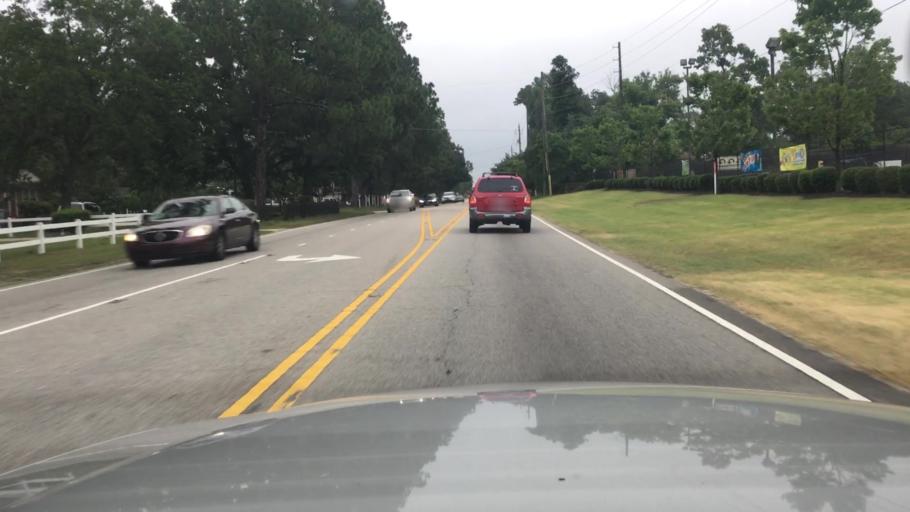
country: US
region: North Carolina
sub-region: Cumberland County
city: Hope Mills
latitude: 34.9822
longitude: -78.9727
